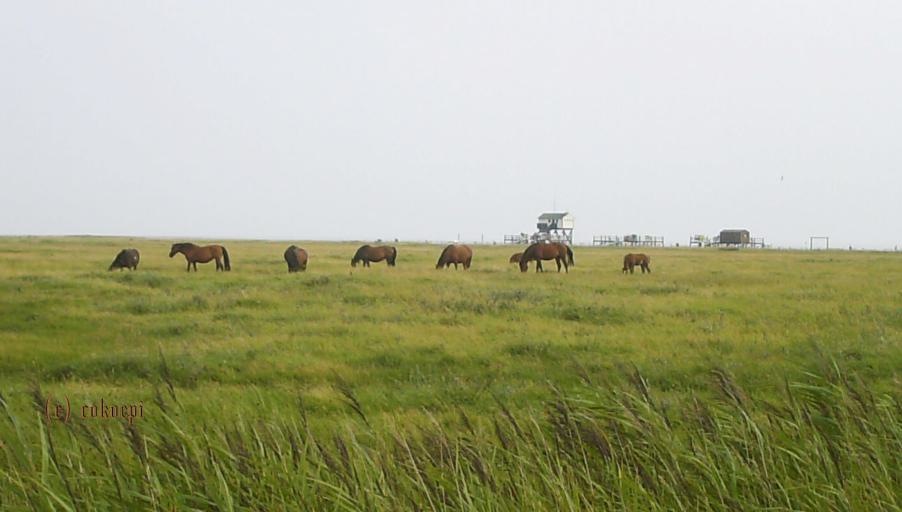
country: DE
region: Schleswig-Holstein
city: Sankt Peter-Ording
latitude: 54.2989
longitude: 8.6208
